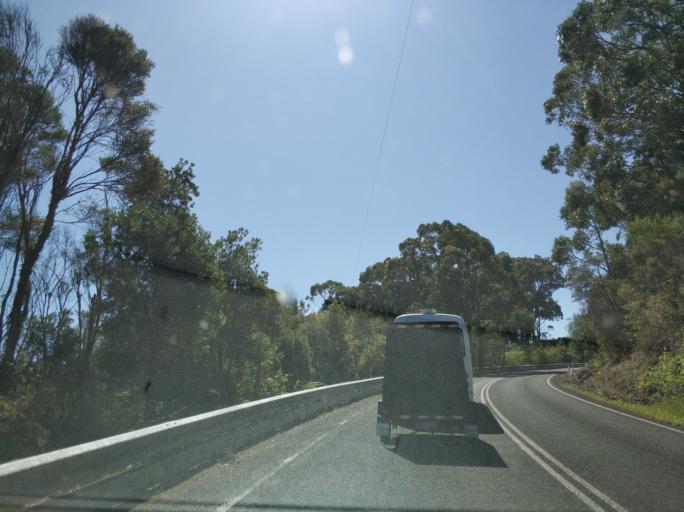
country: AU
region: Victoria
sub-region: Colac-Otway
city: Apollo Bay
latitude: -38.7266
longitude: 143.2485
